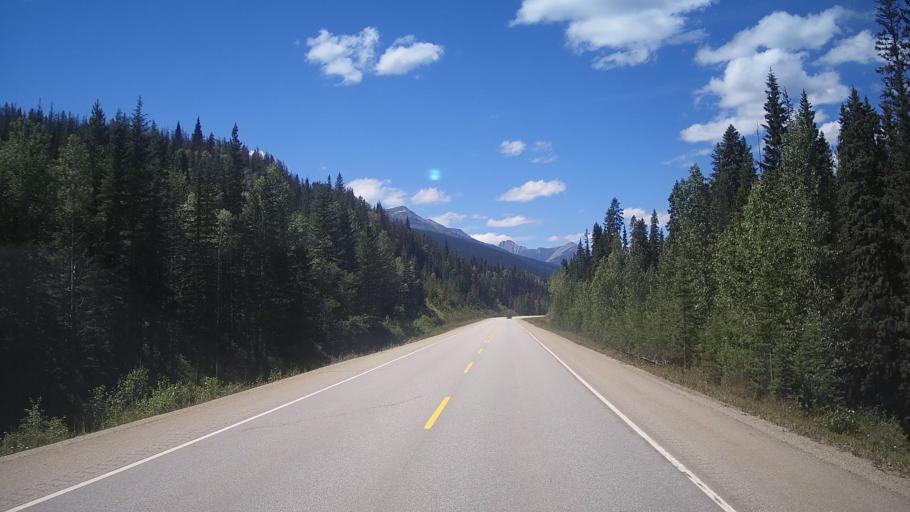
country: CA
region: Alberta
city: Jasper Park Lodge
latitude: 52.8534
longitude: -118.6125
